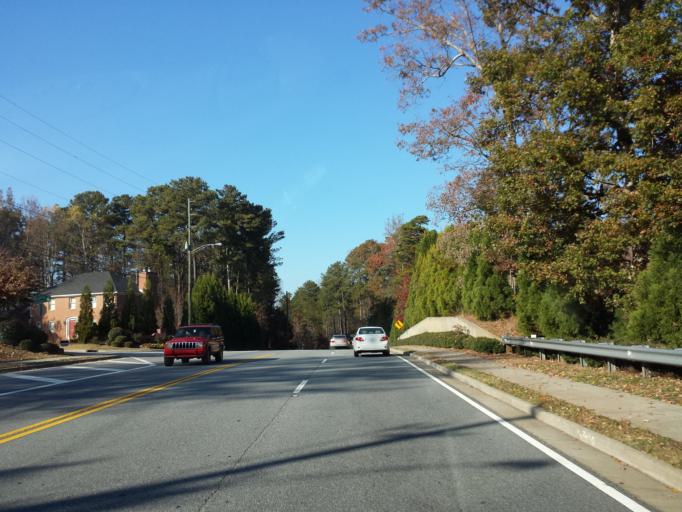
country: US
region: Georgia
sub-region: Cobb County
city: Smyrna
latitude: 33.9486
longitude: -84.4620
